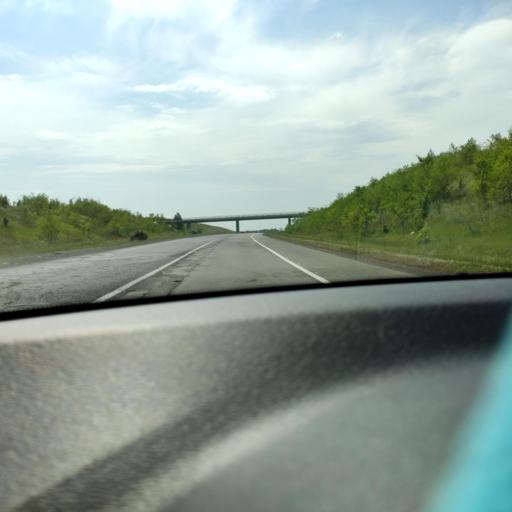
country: RU
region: Samara
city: Petra-Dubrava
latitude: 53.3005
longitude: 50.4104
